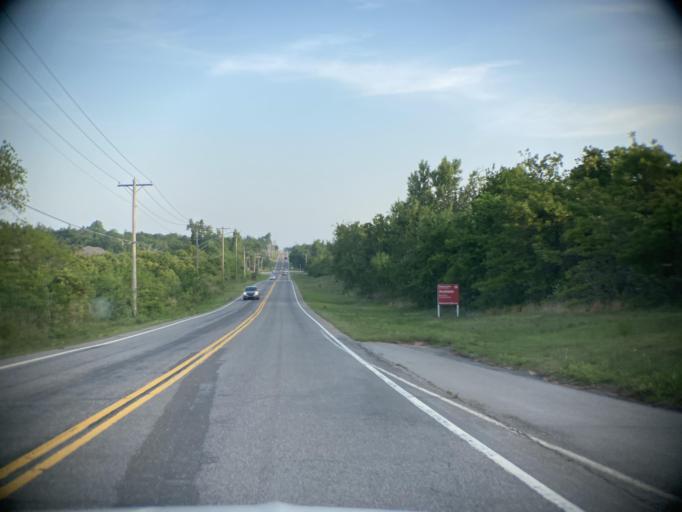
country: US
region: Oklahoma
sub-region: Oklahoma County
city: Nicoma Park
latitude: 35.4473
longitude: -97.3358
